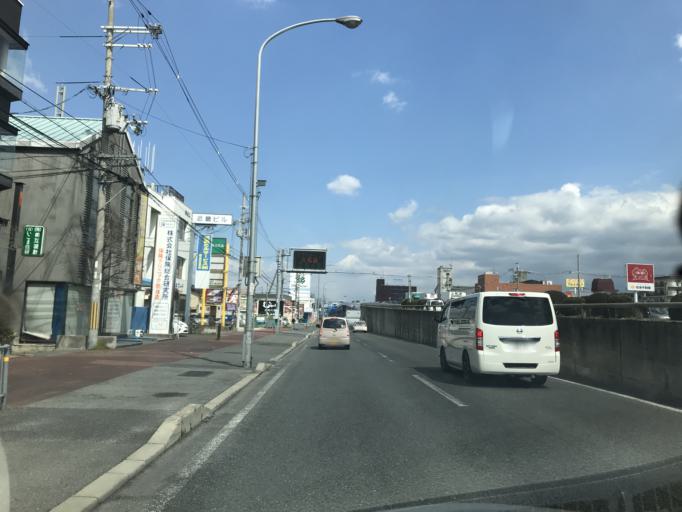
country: JP
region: Nara
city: Nara-shi
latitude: 34.6794
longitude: 135.8002
